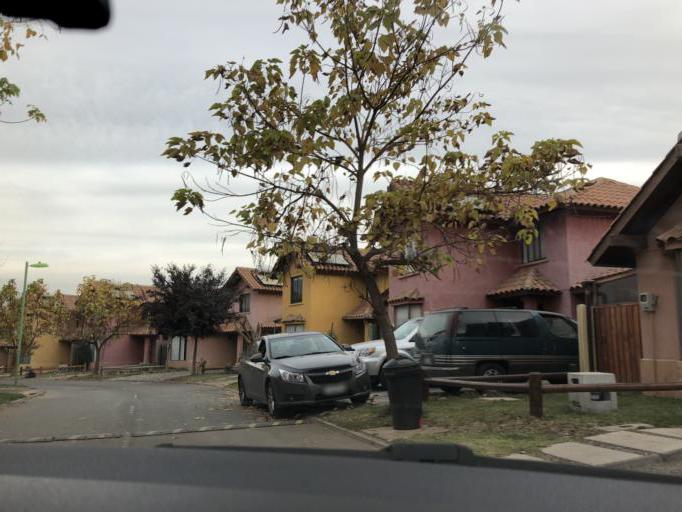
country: CL
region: Santiago Metropolitan
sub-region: Provincia de Cordillera
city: Puente Alto
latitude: -33.5895
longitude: -70.5133
